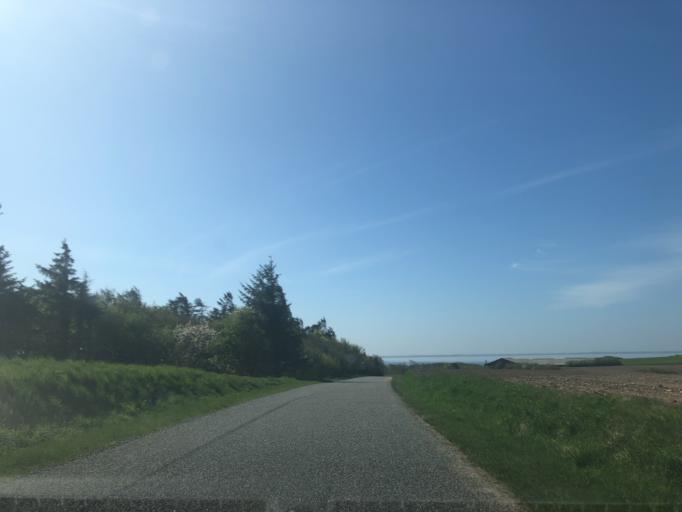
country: DK
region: Central Jutland
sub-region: Holstebro Kommune
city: Vinderup
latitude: 56.5694
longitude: 8.7679
